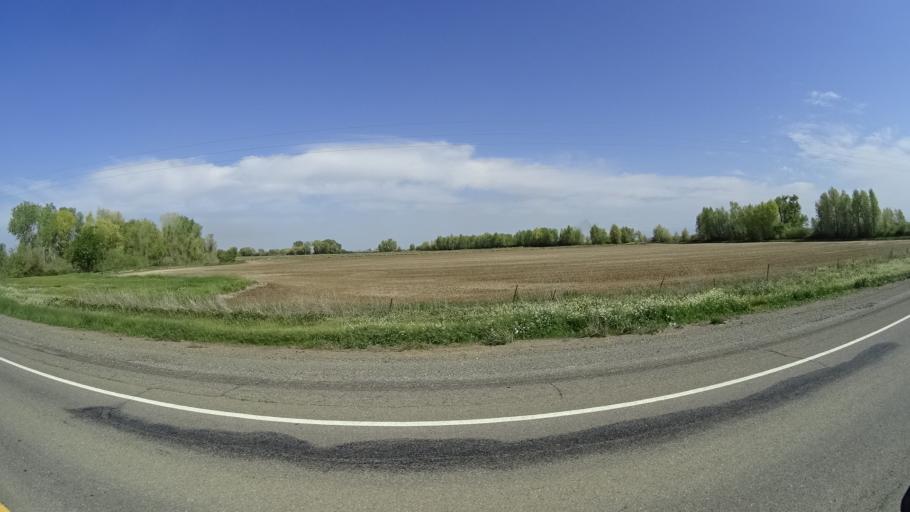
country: US
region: California
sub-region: Butte County
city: Biggs
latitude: 39.4638
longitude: -121.9197
